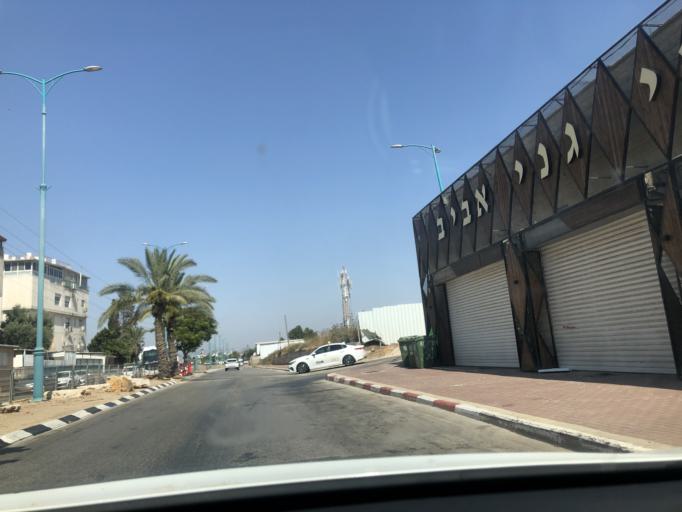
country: IL
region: Central District
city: Lod
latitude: 31.9567
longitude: 34.8808
